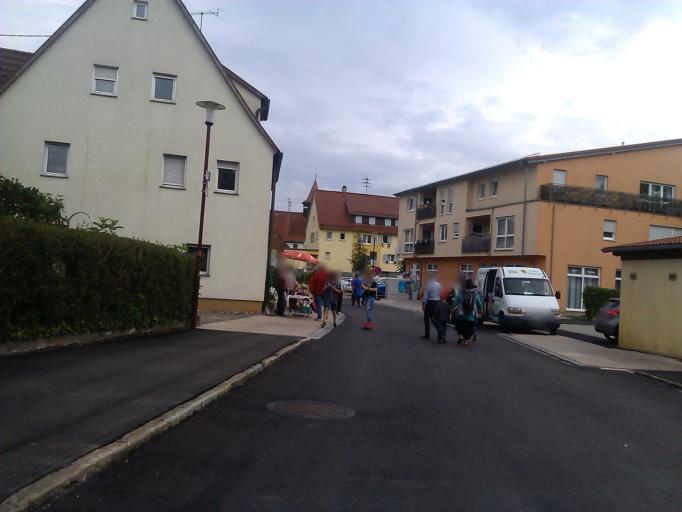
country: DE
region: Baden-Wuerttemberg
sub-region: Regierungsbezirk Stuttgart
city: Fichtenberg
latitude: 48.9861
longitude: 9.7113
